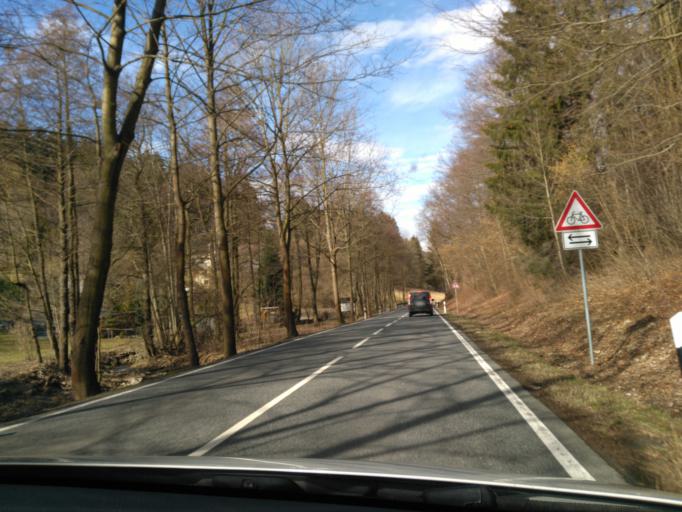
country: DE
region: Saxony
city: Wolkenstein
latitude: 50.6615
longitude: 13.0754
